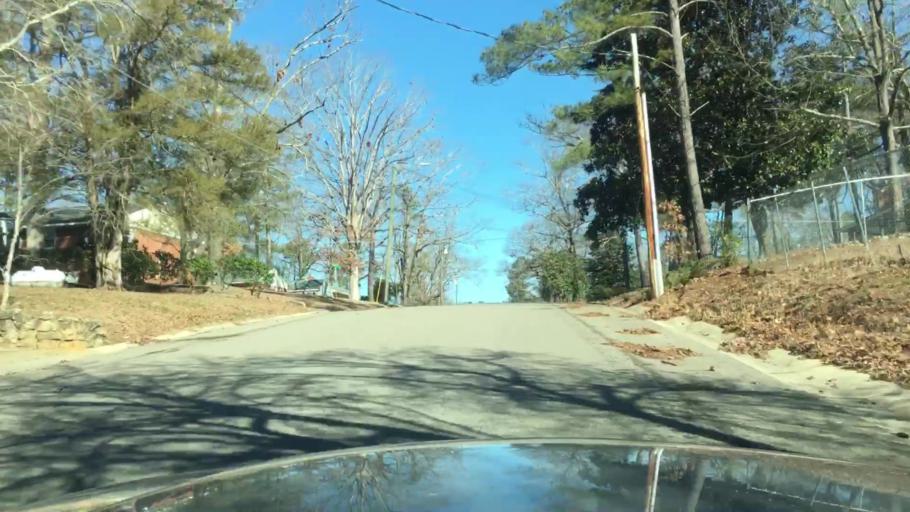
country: US
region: North Carolina
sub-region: Cumberland County
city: Fayetteville
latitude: 35.0768
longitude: -78.9193
